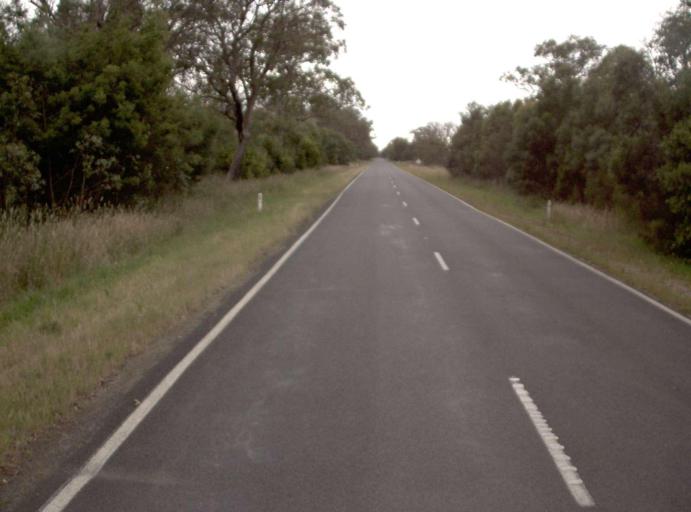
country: AU
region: Victoria
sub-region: Latrobe
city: Traralgon
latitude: -38.5582
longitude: 146.8089
